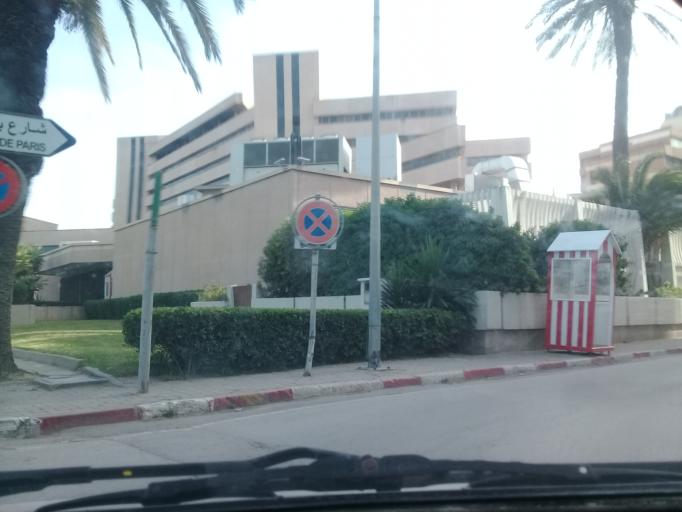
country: TN
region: Tunis
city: Tunis
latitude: 36.8046
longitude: 10.1855
